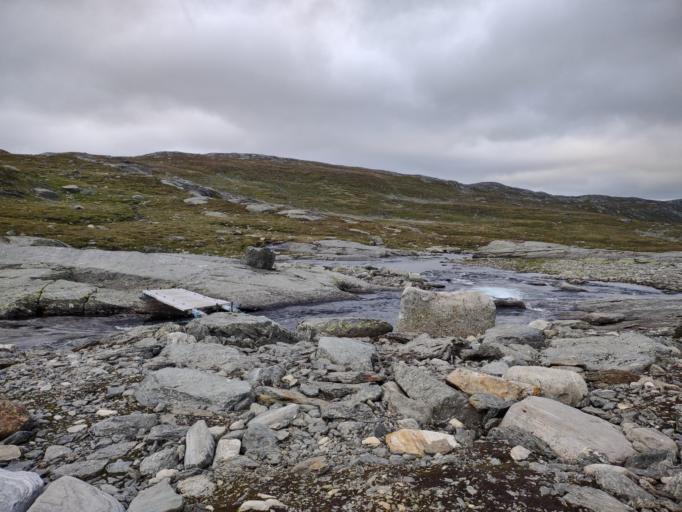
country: NO
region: Aust-Agder
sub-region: Bykle
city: Hovden
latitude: 59.9211
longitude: 7.2084
